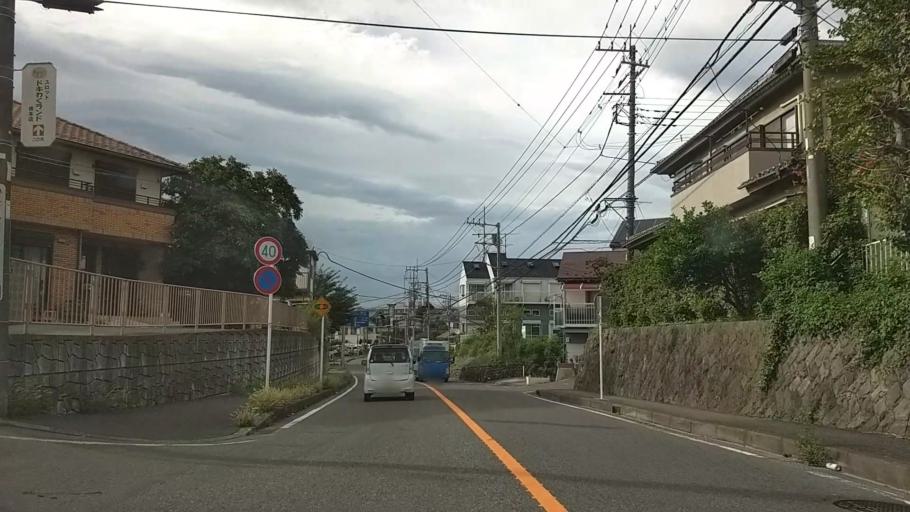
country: JP
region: Tokyo
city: Hachioji
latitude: 35.5698
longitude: 139.3415
